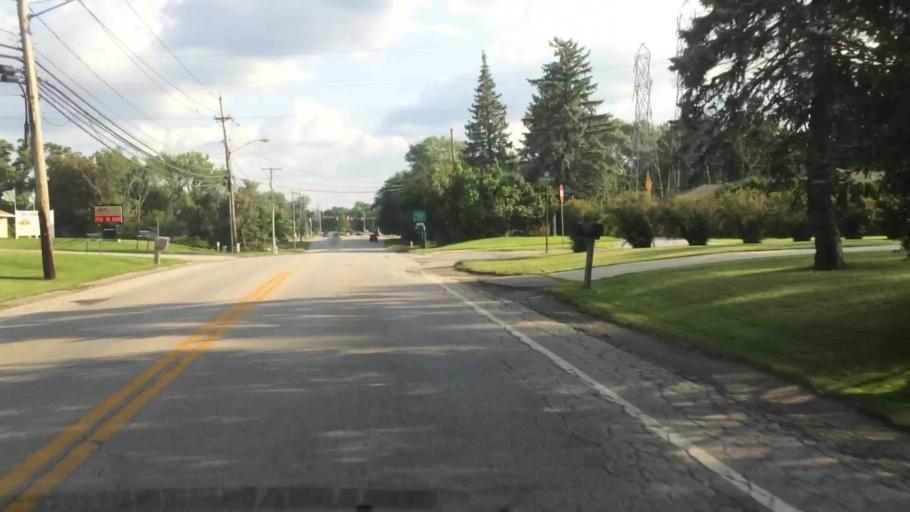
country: US
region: Ohio
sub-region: Cuyahoga County
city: Parma Heights
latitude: 41.3538
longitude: -81.7598
